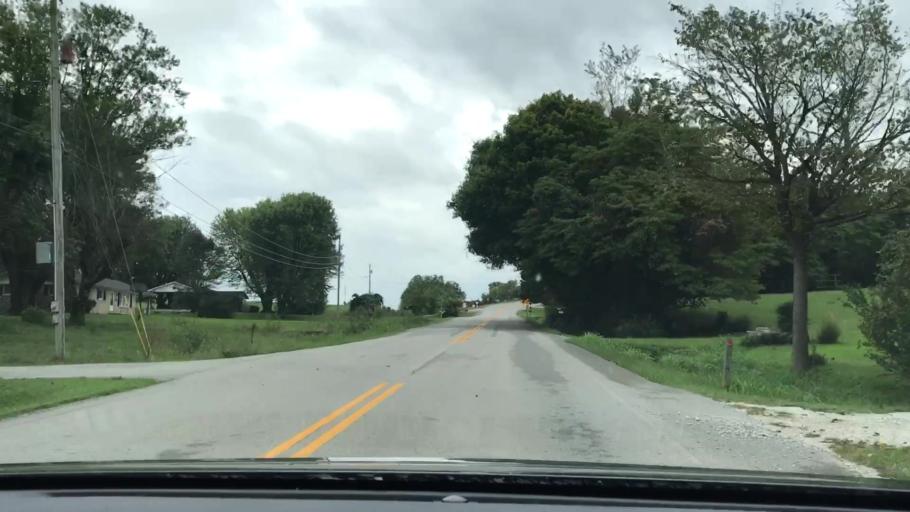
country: US
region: Kentucky
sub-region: Barren County
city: Glasgow
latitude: 36.9597
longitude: -85.8644
